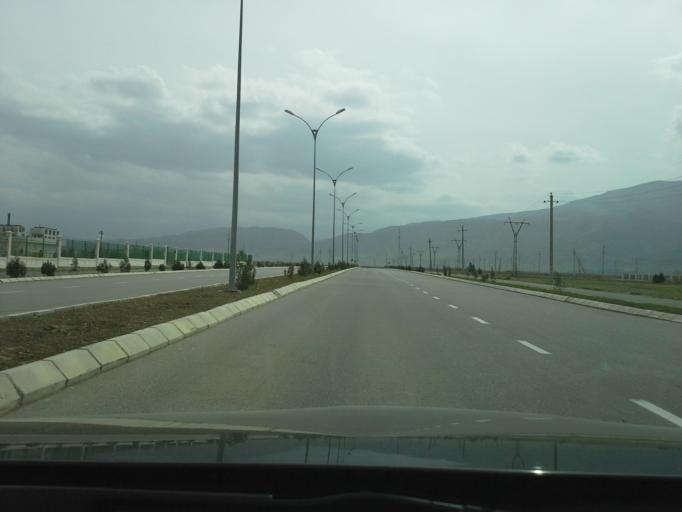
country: TM
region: Ahal
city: Abadan
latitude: 38.0531
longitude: 58.1448
